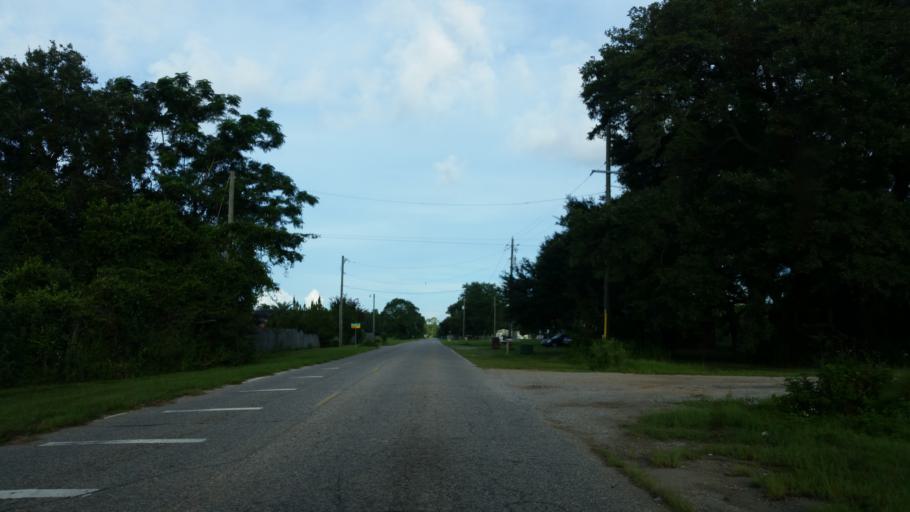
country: US
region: Florida
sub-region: Escambia County
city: Bellview
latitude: 30.4760
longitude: -87.3149
